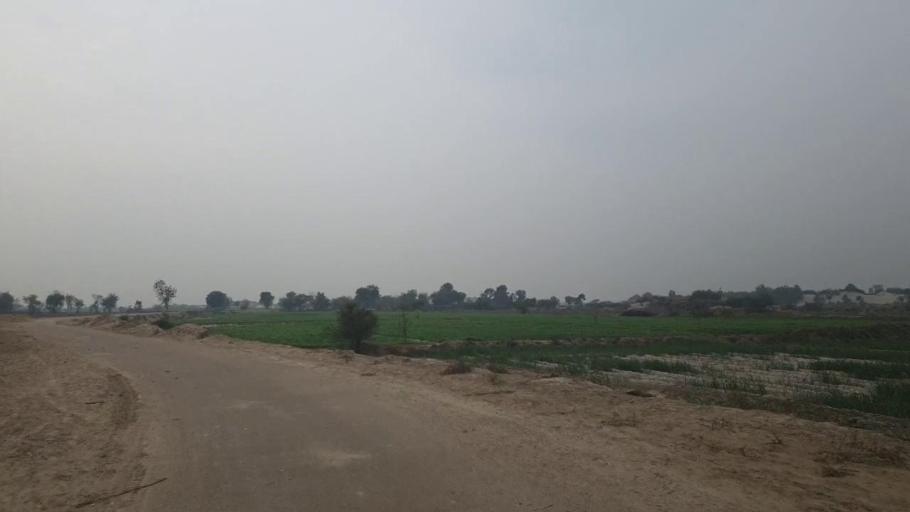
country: PK
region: Sindh
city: Tando Adam
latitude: 25.7356
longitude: 68.6973
